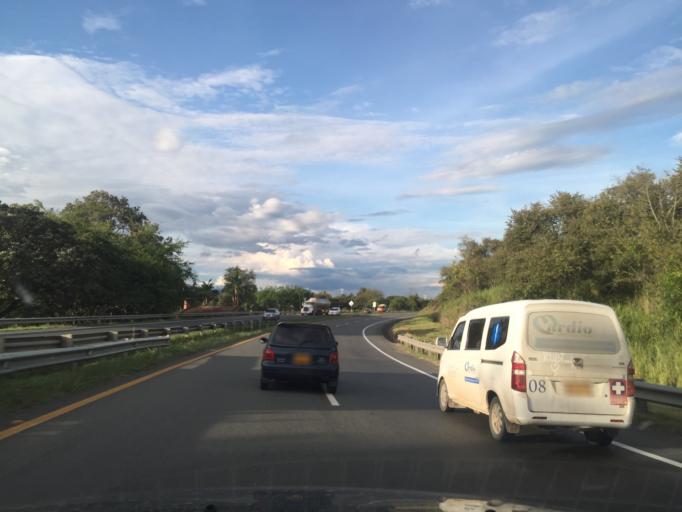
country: CO
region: Valle del Cauca
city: Bugalagrande
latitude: 4.2146
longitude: -76.1500
